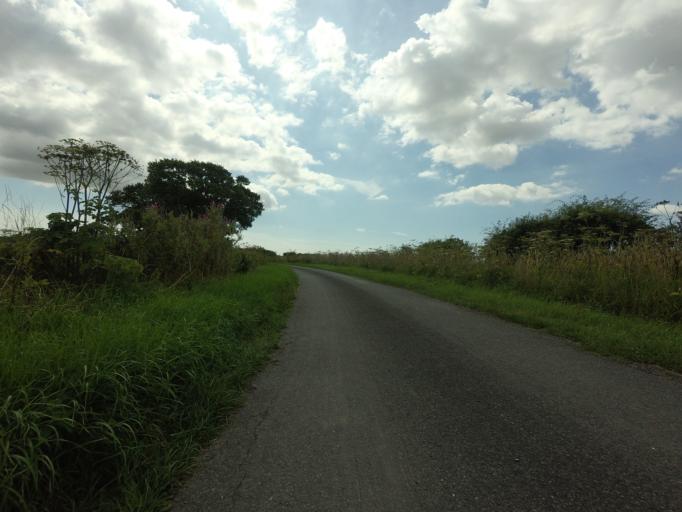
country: GB
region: England
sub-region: Kent
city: Stone
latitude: 51.0560
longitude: 0.7607
